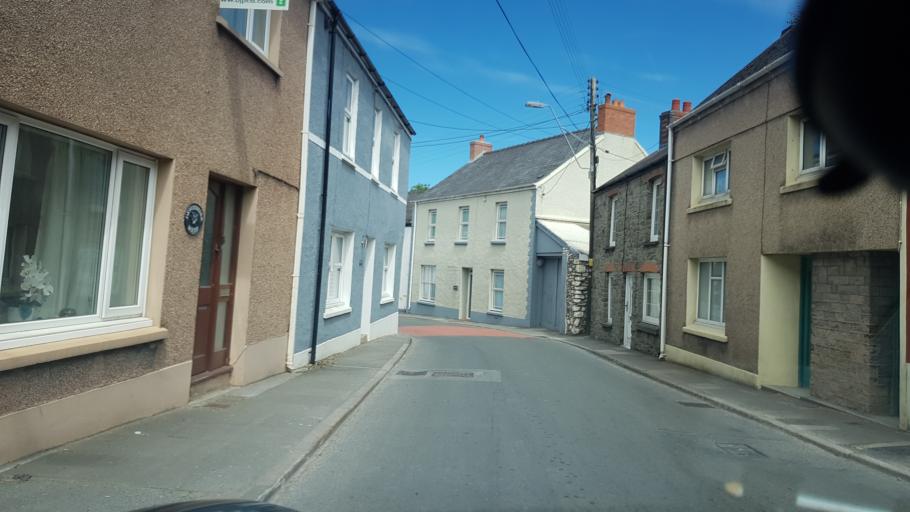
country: GB
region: Wales
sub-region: Carmarthenshire
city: Saint Clears
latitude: 51.7681
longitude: -4.4635
